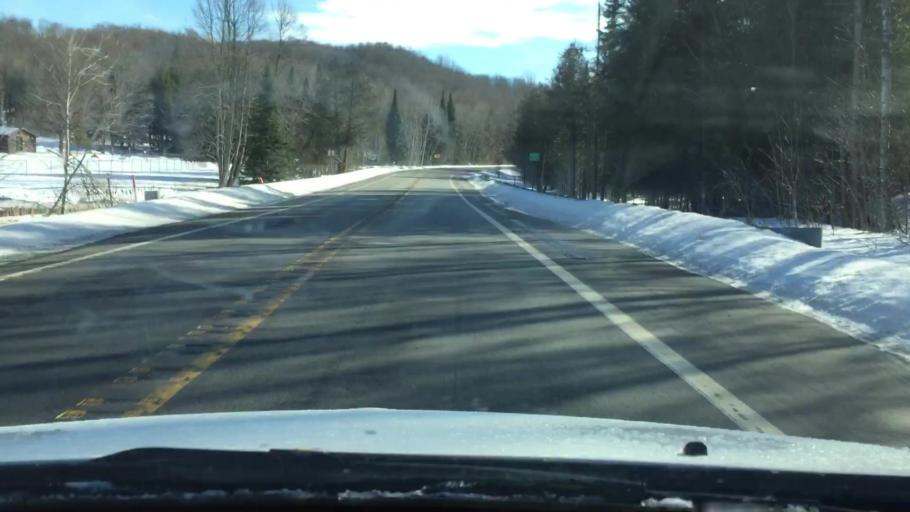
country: US
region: Michigan
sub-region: Antrim County
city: Mancelona
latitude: 45.0071
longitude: -85.0640
